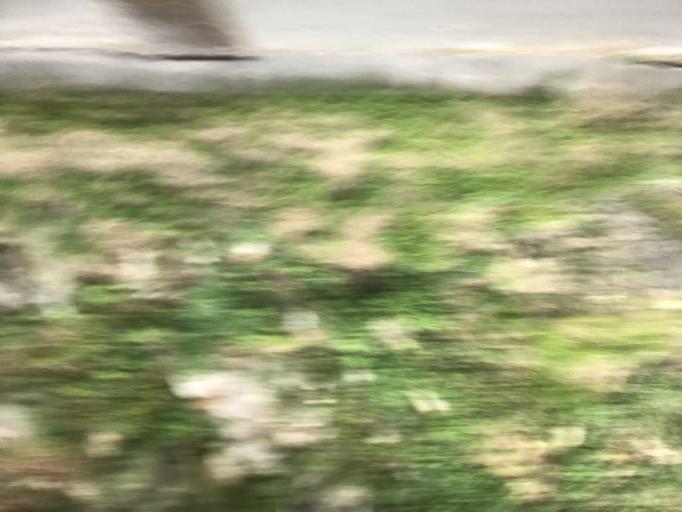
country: ES
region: Basque Country
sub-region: Provincia de Guipuzcoa
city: Villabona
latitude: 43.1870
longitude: -2.0515
